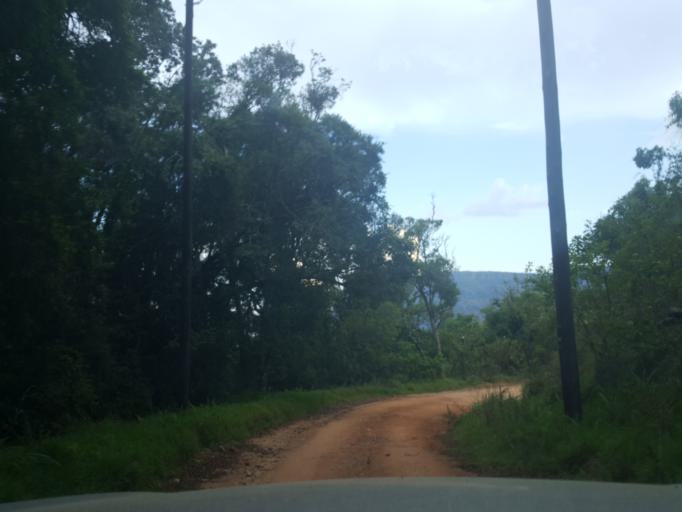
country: ZA
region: Limpopo
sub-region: Mopani District Municipality
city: Hoedspruit
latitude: -24.5757
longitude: 30.8658
